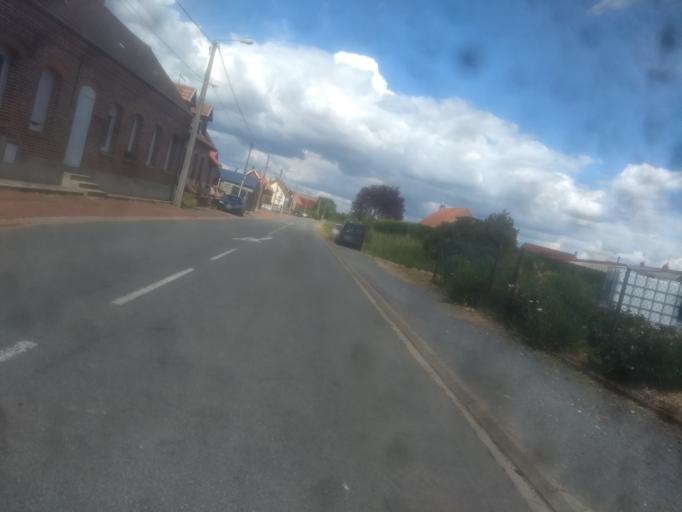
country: FR
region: Nord-Pas-de-Calais
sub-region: Departement du Pas-de-Calais
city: Croisilles
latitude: 50.2259
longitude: 2.8357
